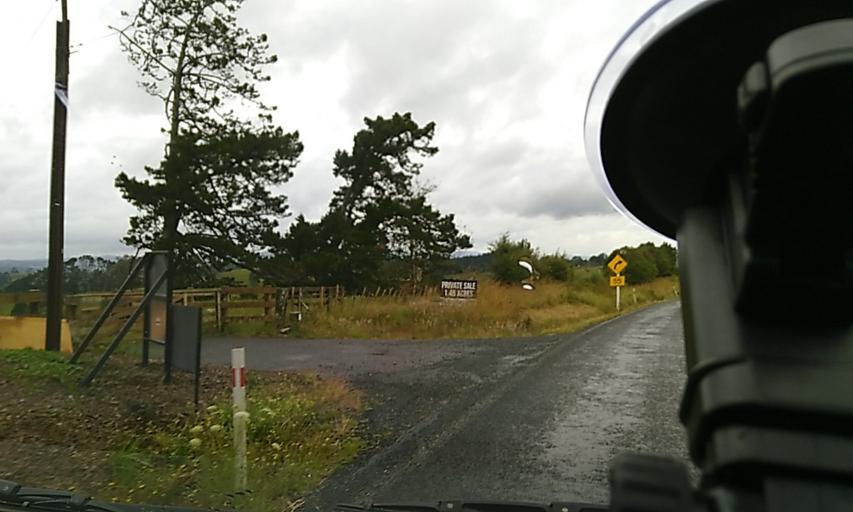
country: NZ
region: Auckland
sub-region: Auckland
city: Pukekohe East
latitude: -37.3208
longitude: 174.9218
